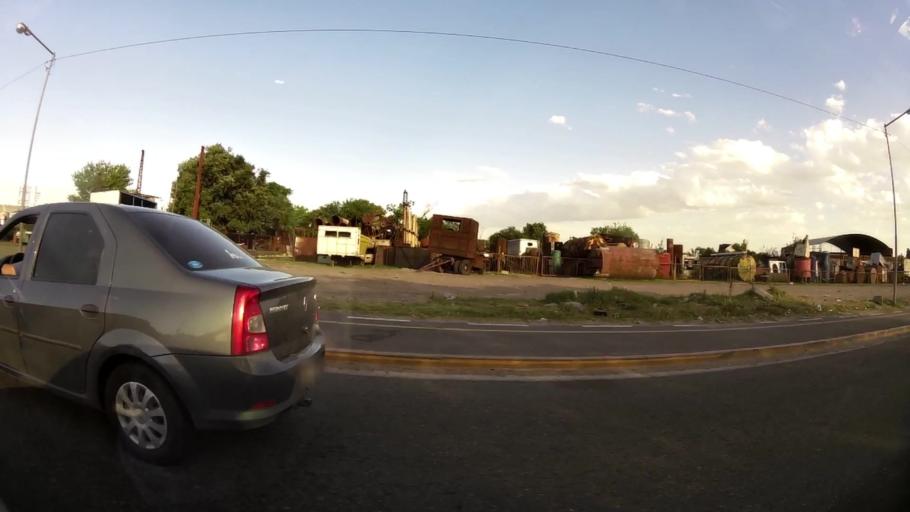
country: AR
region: Buenos Aires
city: Caseros
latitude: -34.5536
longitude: -58.5848
